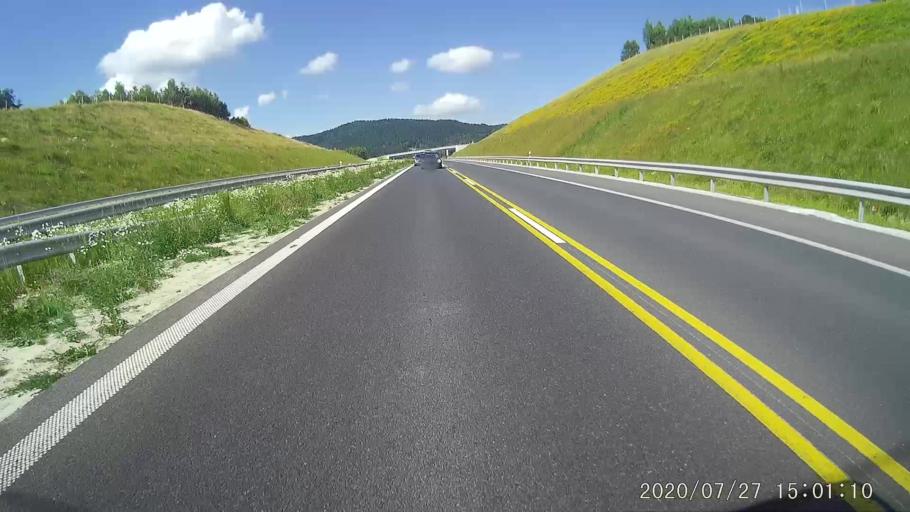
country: PL
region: Lesser Poland Voivodeship
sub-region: Powiat suski
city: Letownia
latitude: 49.6857
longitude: 19.8949
